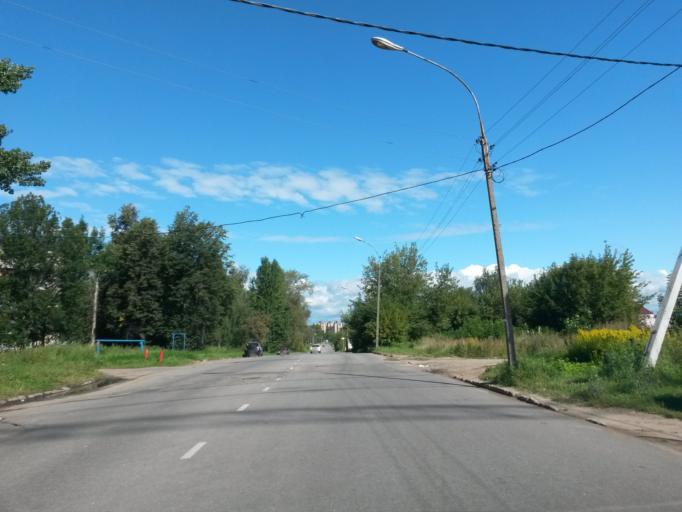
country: RU
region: Jaroslavl
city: Yaroslavl
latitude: 57.5811
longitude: 39.8658
